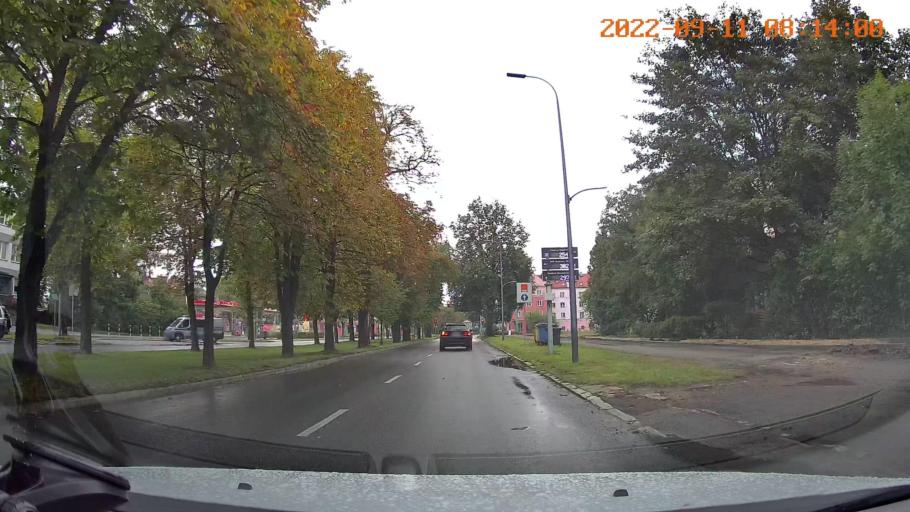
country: PL
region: Silesian Voivodeship
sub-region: Tychy
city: Tychy
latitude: 50.1225
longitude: 18.9862
